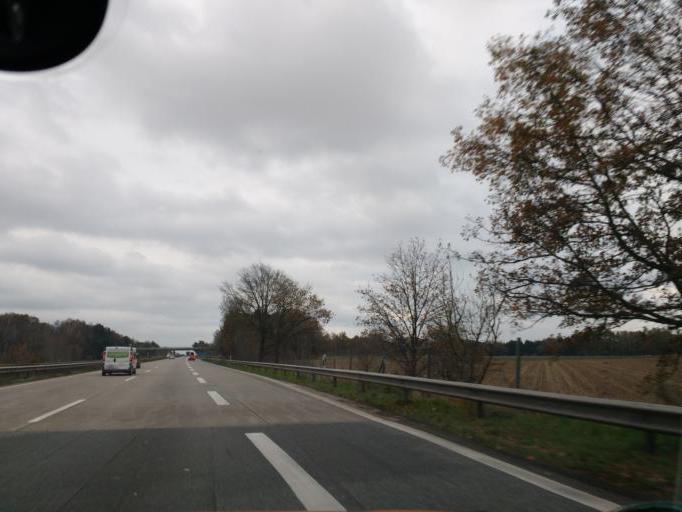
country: DE
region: Lower Saxony
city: Verden
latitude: 52.9625
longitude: 9.2415
